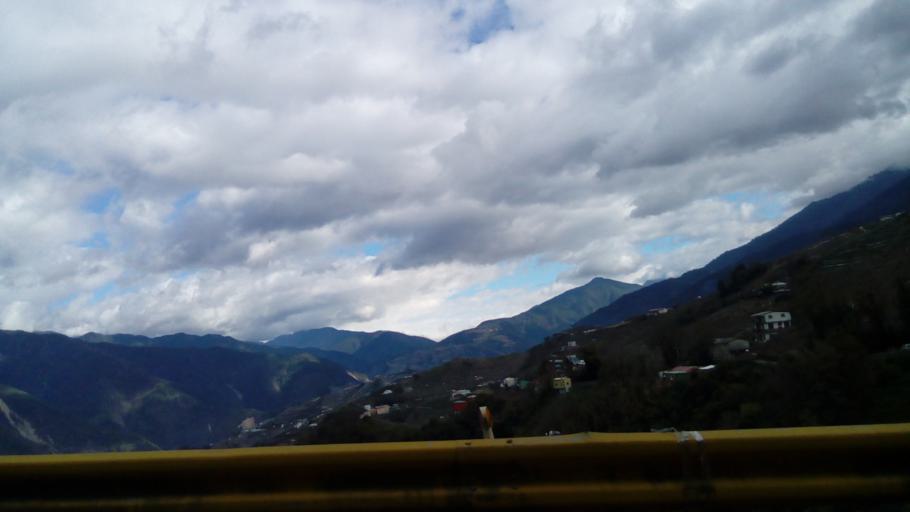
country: TW
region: Taiwan
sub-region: Nantou
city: Puli
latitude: 24.2550
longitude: 121.2525
